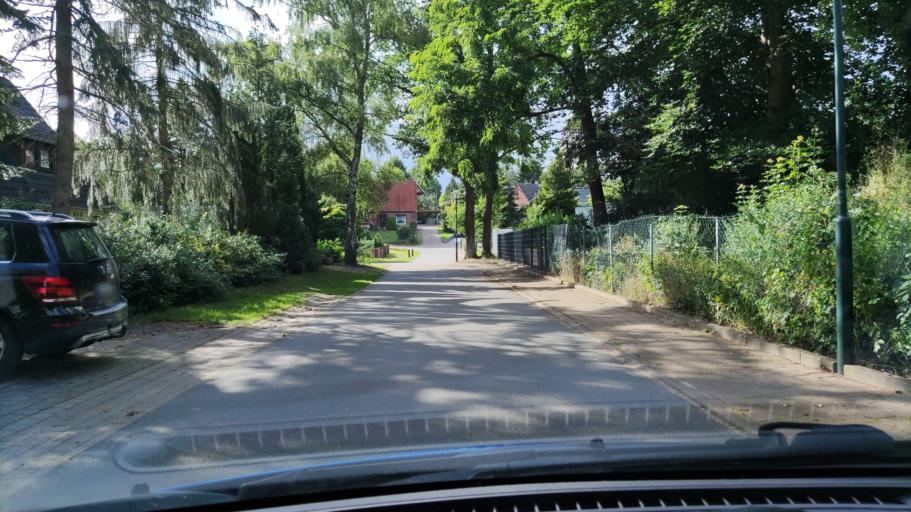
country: DE
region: Lower Saxony
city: Salzhausen
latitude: 53.2252
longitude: 10.1519
